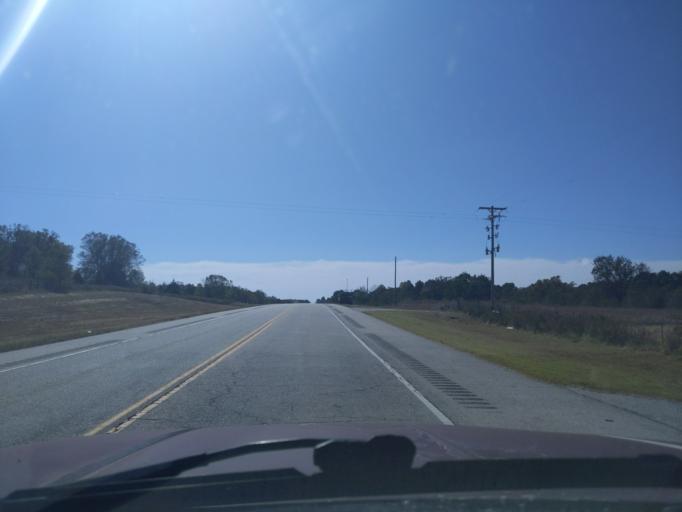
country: US
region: Oklahoma
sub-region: Creek County
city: Bristow
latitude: 35.7407
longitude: -96.3872
